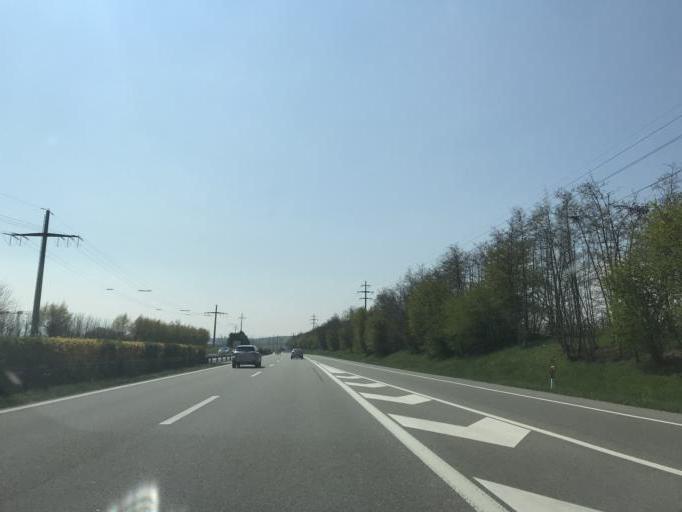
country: CH
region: Vaud
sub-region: Nyon District
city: Trelex
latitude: 46.3925
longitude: 6.2075
